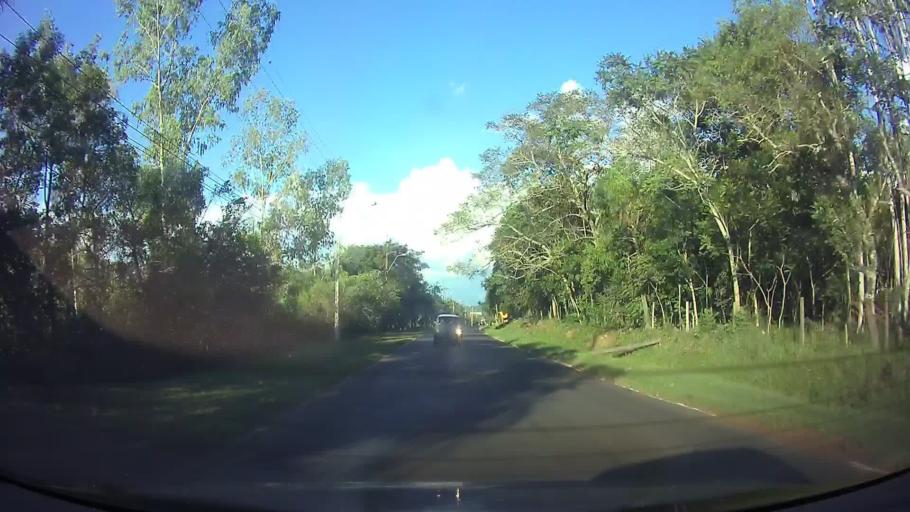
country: PY
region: Cordillera
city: Emboscada
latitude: -25.1944
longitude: -57.3161
